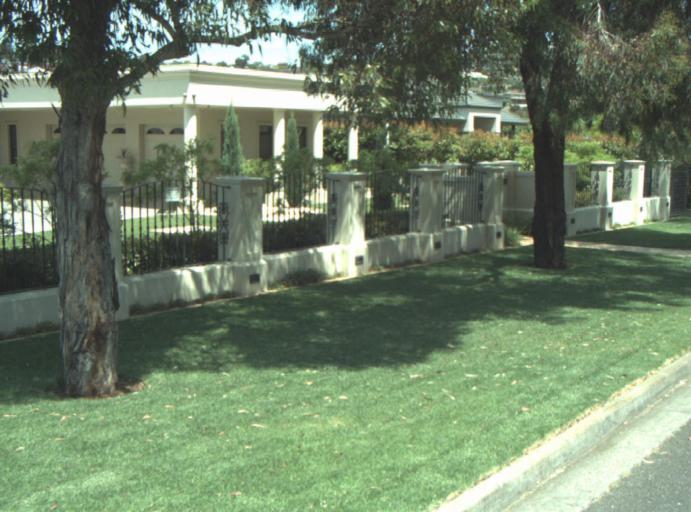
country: AU
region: Victoria
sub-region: Greater Geelong
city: Wandana Heights
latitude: -38.1601
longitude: 144.3264
